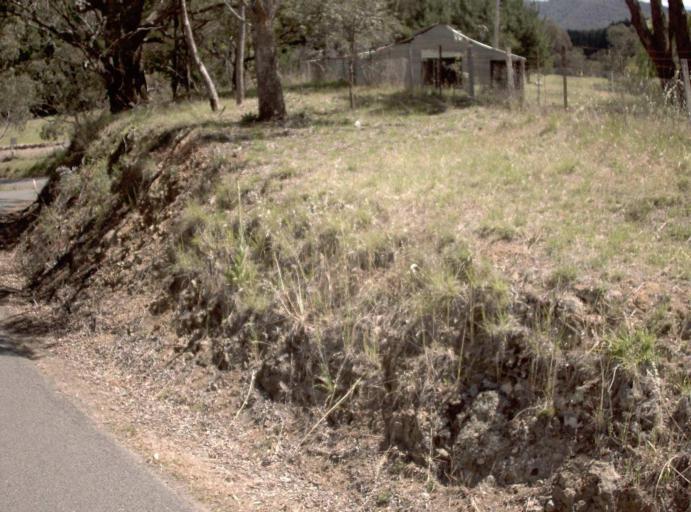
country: AU
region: New South Wales
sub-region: Bombala
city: Bombala
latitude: -37.0971
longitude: 148.6243
